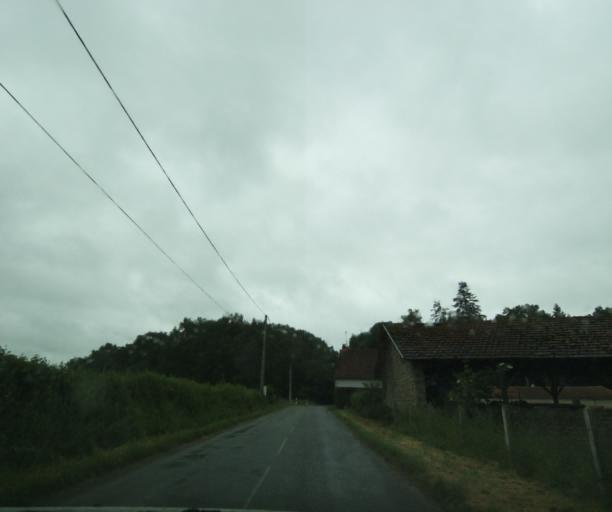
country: FR
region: Bourgogne
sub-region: Departement de Saone-et-Loire
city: Palinges
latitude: 46.5219
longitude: 4.2119
